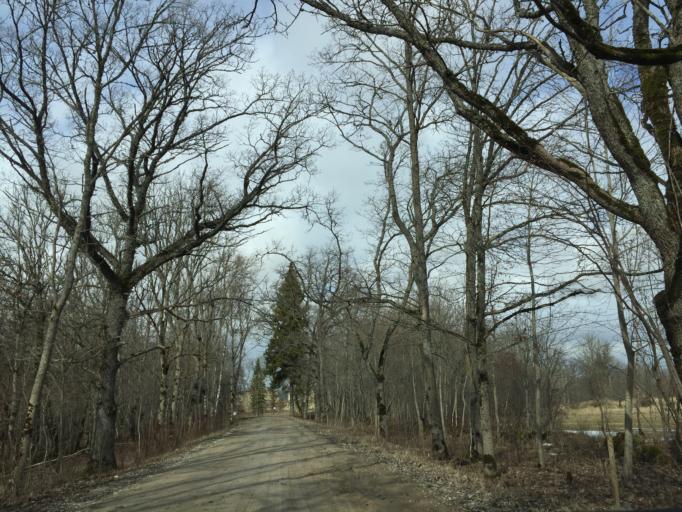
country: EE
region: Laeaene
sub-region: Lihula vald
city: Lihula
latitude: 58.7378
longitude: 23.8329
